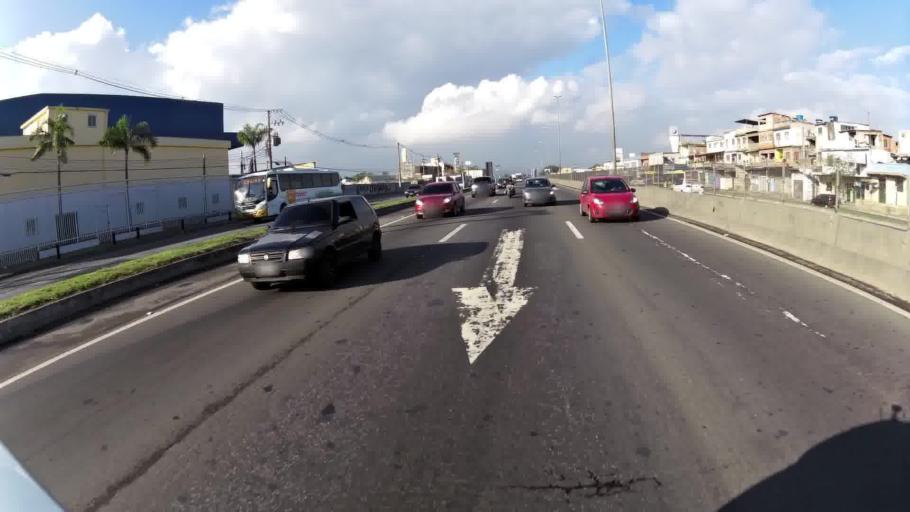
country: BR
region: Rio de Janeiro
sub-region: Duque De Caxias
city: Duque de Caxias
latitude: -22.7962
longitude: -43.2886
